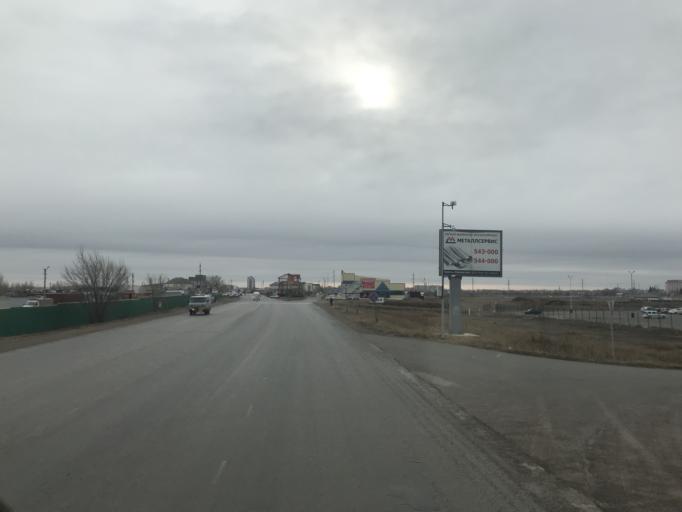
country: KZ
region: Batys Qazaqstan
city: Oral
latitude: 51.2663
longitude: 51.4064
